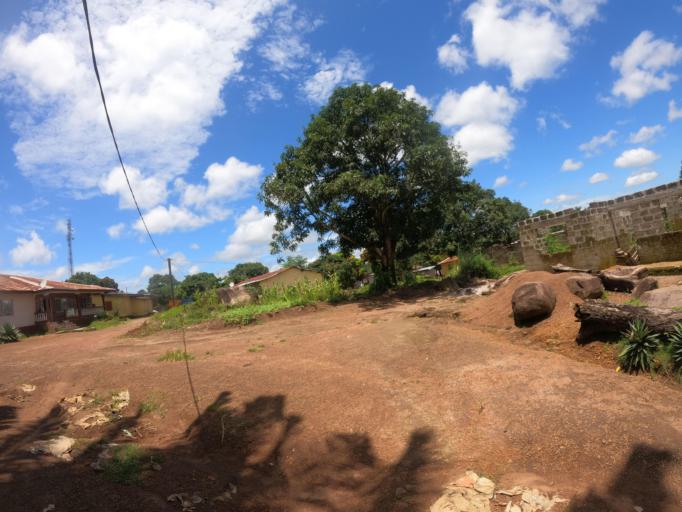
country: SL
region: Northern Province
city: Makeni
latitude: 8.8954
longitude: -12.0638
